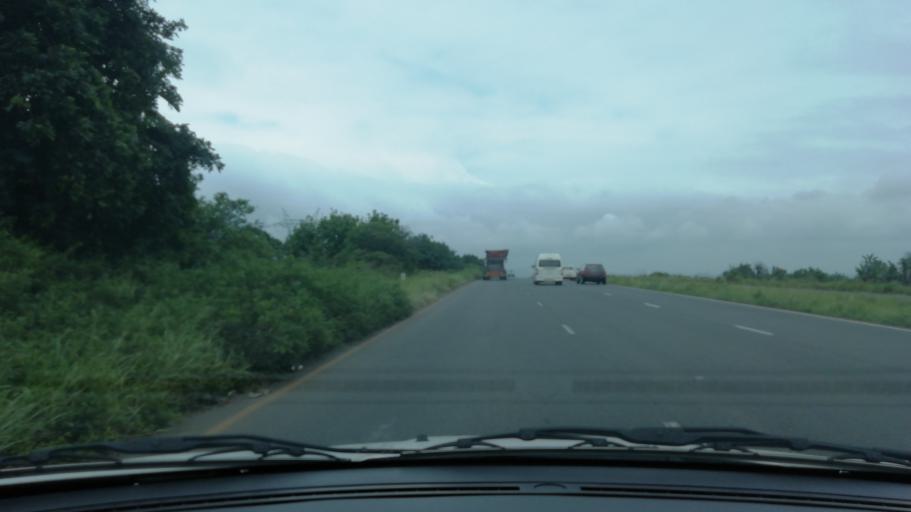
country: ZA
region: KwaZulu-Natal
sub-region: uThungulu District Municipality
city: Richards Bay
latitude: -28.7748
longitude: 32.0085
